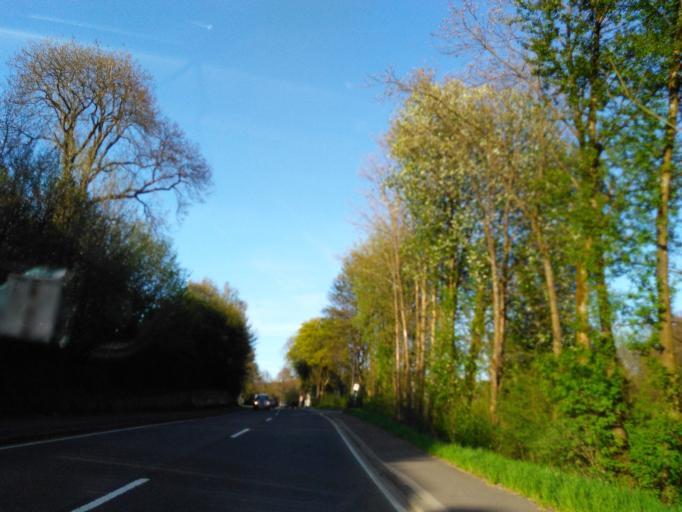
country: DE
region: North Rhine-Westphalia
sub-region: Regierungsbezirk Koln
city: Much
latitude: 50.9175
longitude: 7.4317
